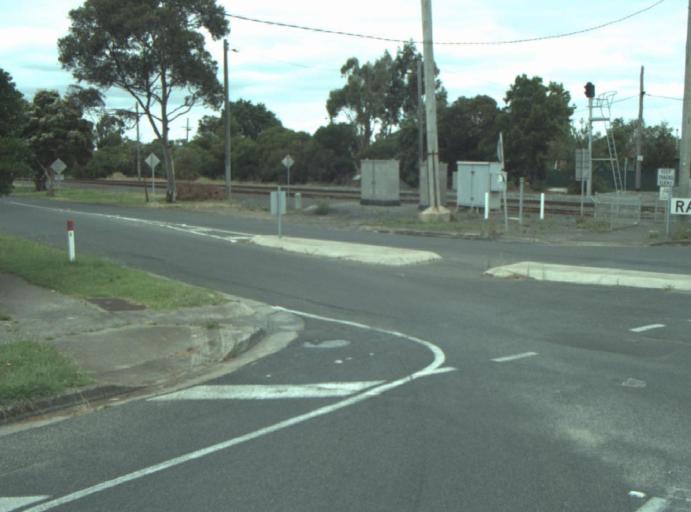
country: AU
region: Victoria
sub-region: Greater Geelong
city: East Geelong
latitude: -38.1609
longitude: 144.3631
